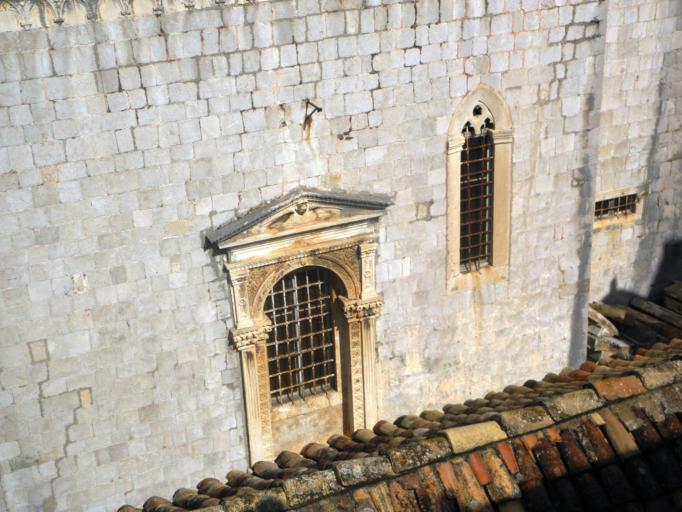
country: HR
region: Dubrovacko-Neretvanska
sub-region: Grad Dubrovnik
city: Dubrovnik
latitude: 42.6410
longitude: 18.1109
